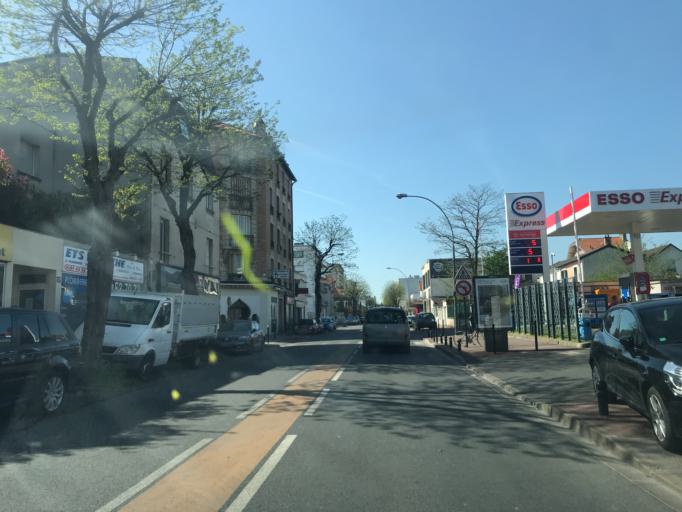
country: FR
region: Ile-de-France
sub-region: Departement du Val-de-Marne
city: Saint-Maur-des-Fosses
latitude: 48.7989
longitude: 2.5004
